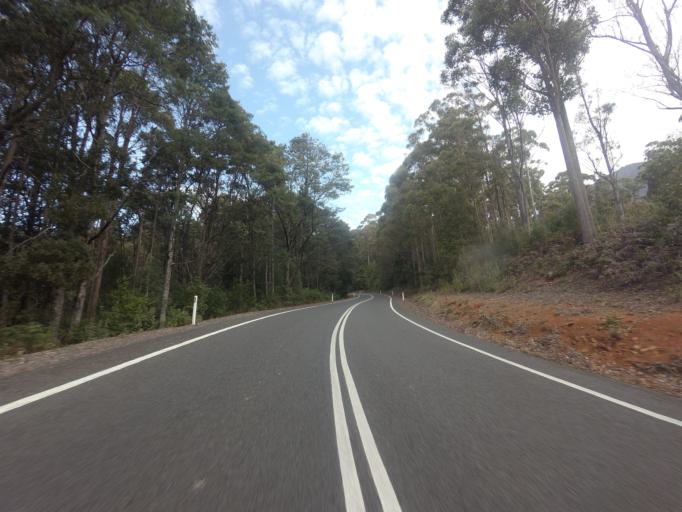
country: AU
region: Tasmania
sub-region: Meander Valley
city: Deloraine
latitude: -41.6415
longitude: 146.7185
